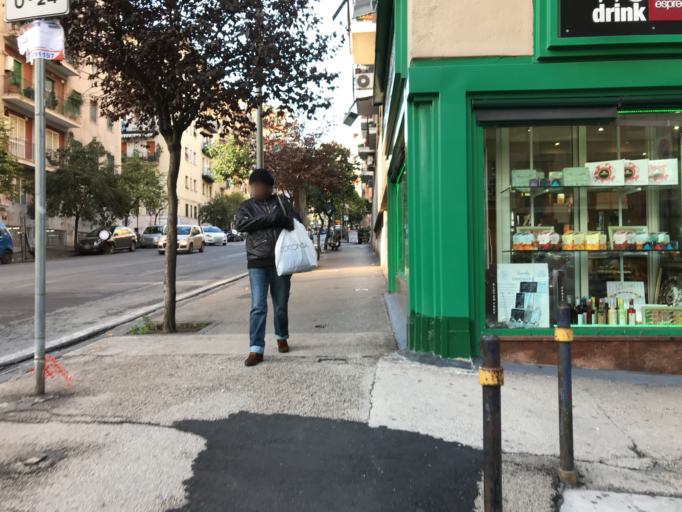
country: IT
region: Campania
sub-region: Provincia di Napoli
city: Napoli
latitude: 40.8517
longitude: 14.2307
